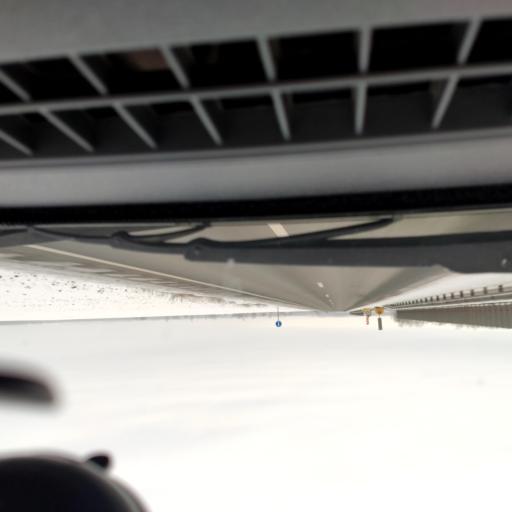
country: RU
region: Bashkortostan
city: Kushnarenkovo
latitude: 55.0639
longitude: 55.3708
